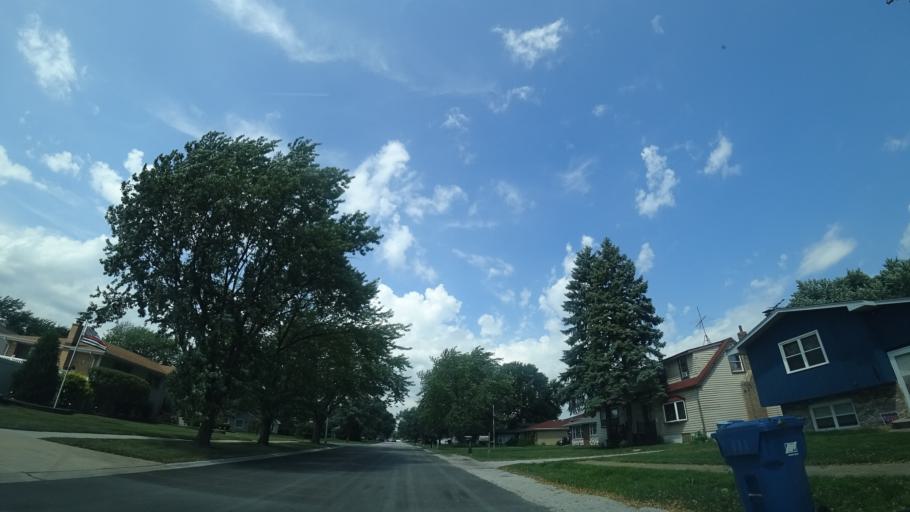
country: US
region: Illinois
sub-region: Cook County
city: Alsip
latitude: 41.6730
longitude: -87.7439
